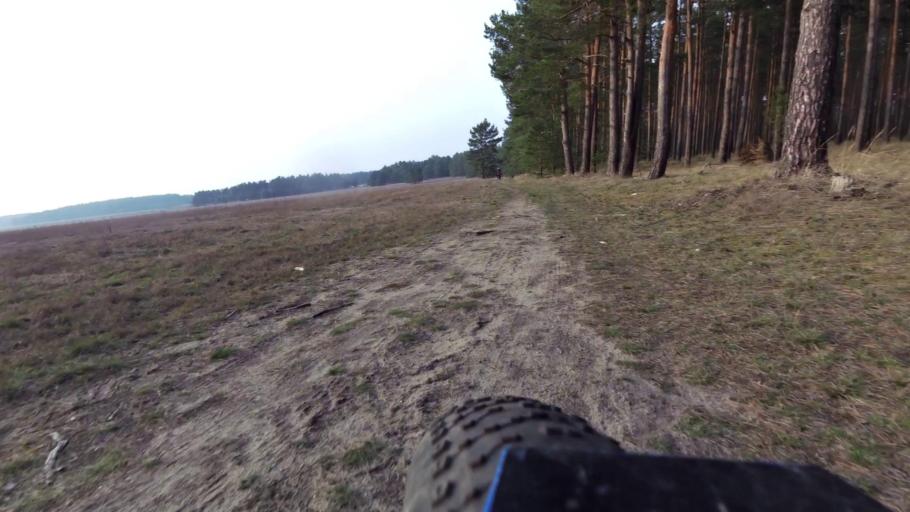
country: DE
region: Brandenburg
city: Vogelsang
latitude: 52.2685
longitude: 14.6890
